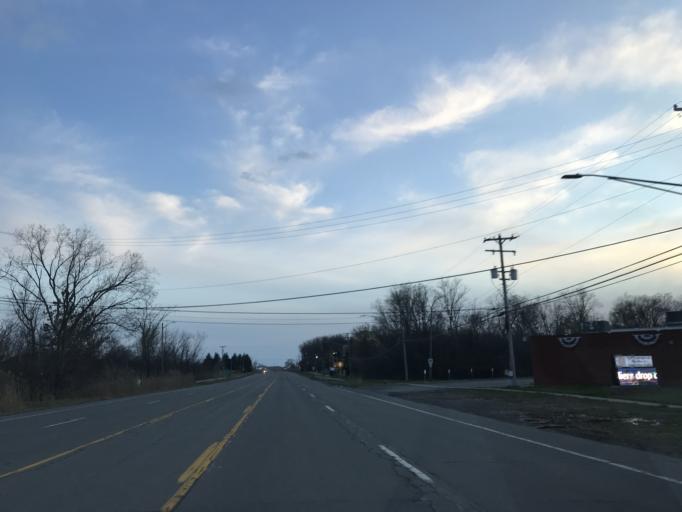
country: US
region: Michigan
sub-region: Wayne County
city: Southgate
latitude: 42.1911
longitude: -83.2204
